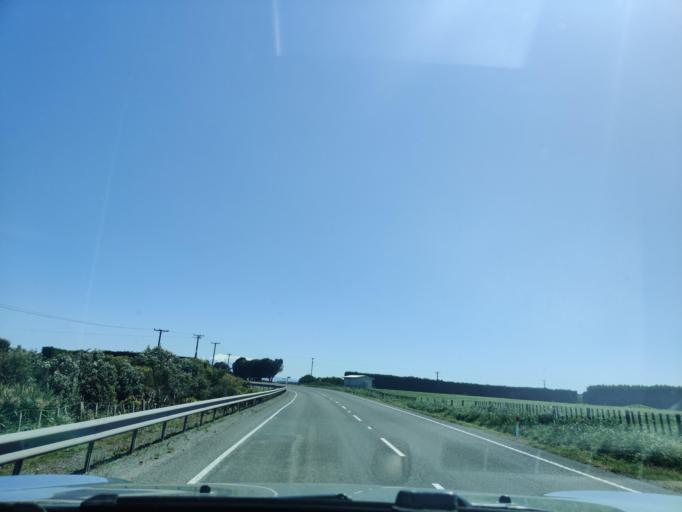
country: NZ
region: Taranaki
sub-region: South Taranaki District
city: Patea
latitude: -39.6659
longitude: 174.4020
